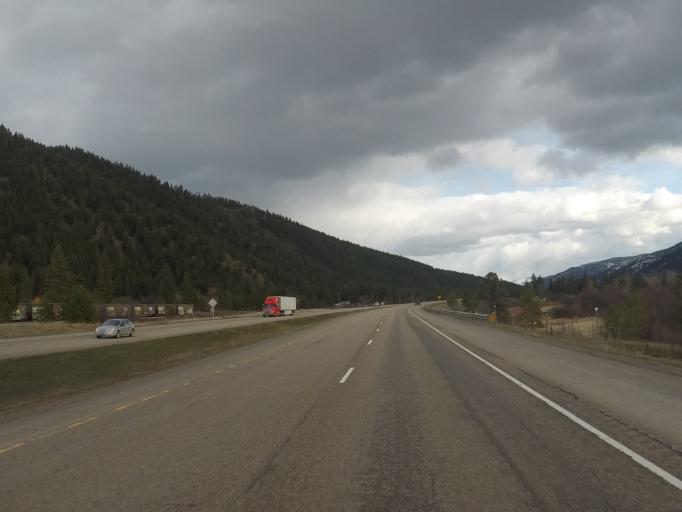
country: US
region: Montana
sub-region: Missoula County
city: Bonner-West Riverside
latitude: 46.8639
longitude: -113.8698
